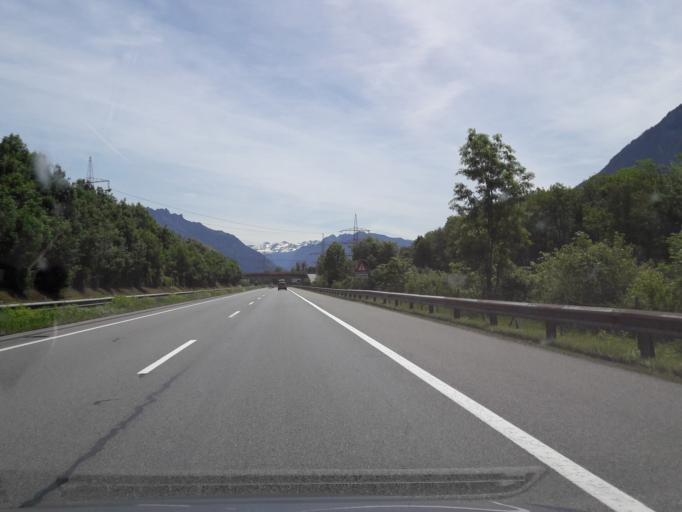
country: AT
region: Vorarlberg
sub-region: Politischer Bezirk Feldkirch
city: Schlins
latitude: 47.1991
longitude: 9.6857
